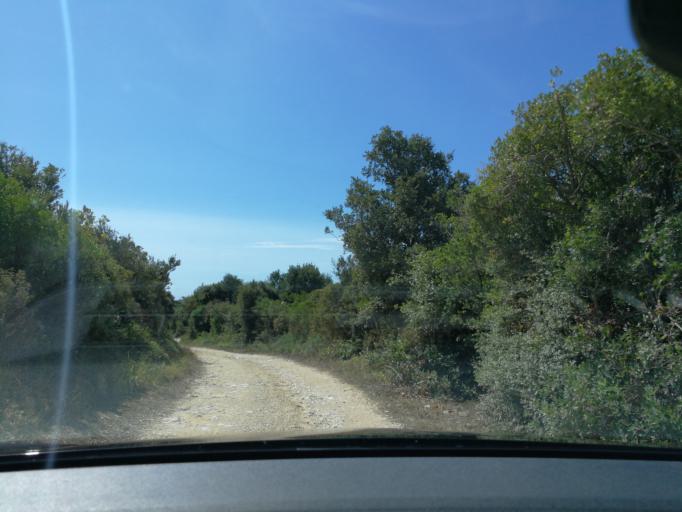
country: HR
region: Istarska
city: Medulin
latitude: 44.8111
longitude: 13.8791
